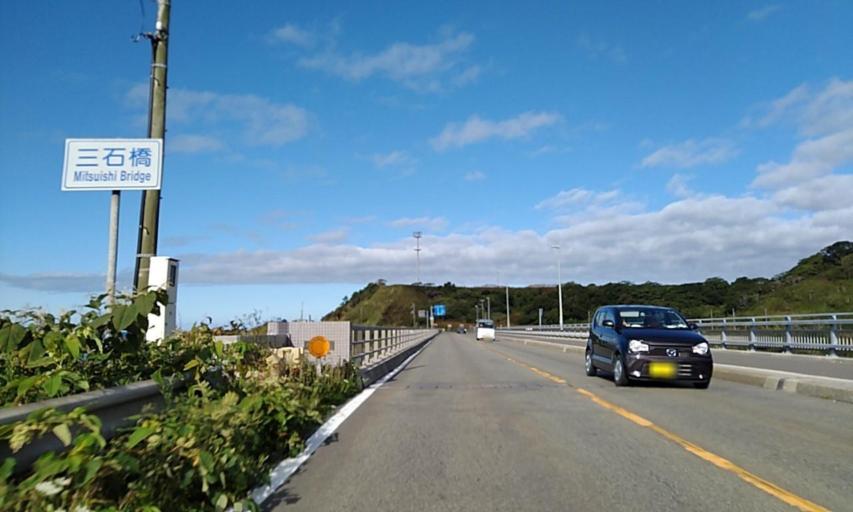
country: JP
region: Hokkaido
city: Shizunai-furukawacho
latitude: 42.2466
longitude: 142.5748
